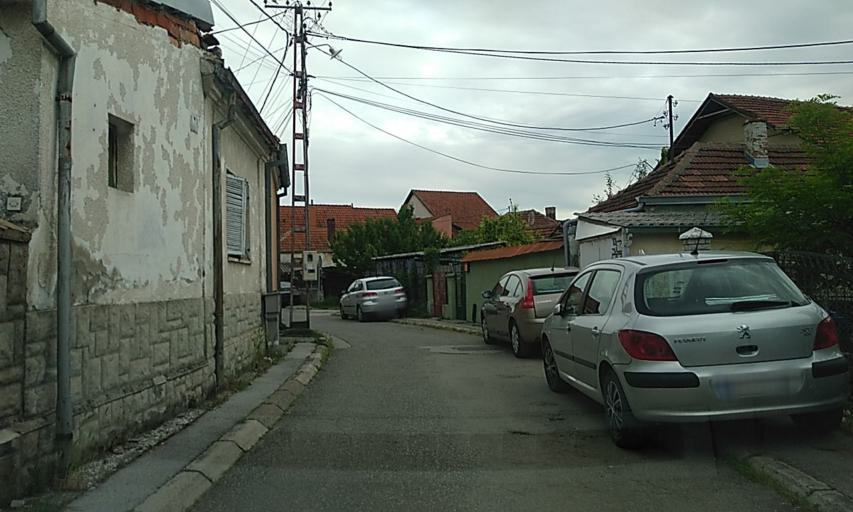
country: RS
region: Central Serbia
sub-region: Nisavski Okrug
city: Nis
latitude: 43.3182
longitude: 21.8836
